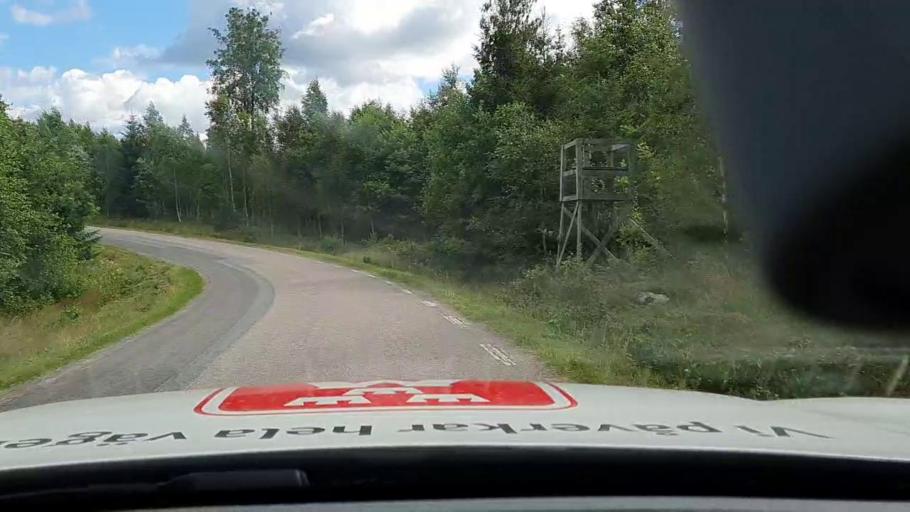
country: SE
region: Vaestra Goetaland
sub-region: Karlsborgs Kommun
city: Molltorp
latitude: 58.6074
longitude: 14.2976
